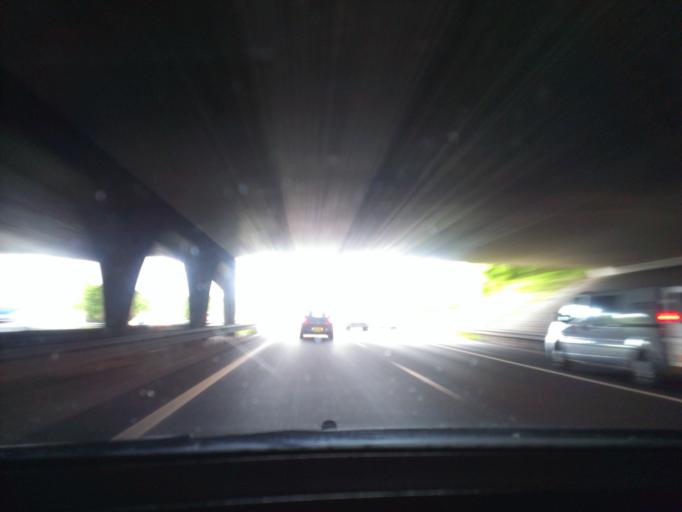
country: NL
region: Gelderland
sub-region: Gemeente Rozendaal
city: Rozendaal
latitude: 52.0662
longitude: 5.9434
